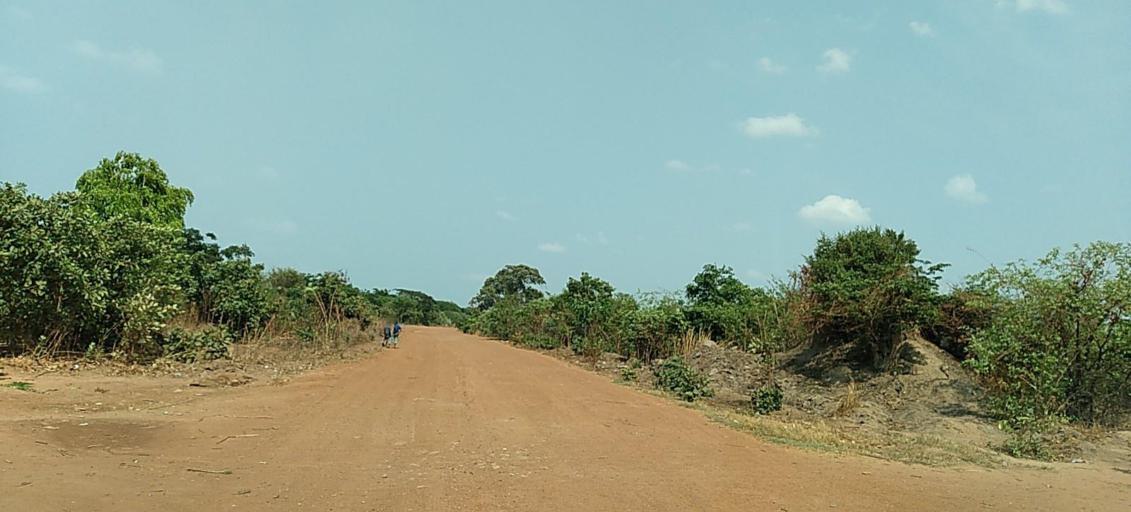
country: ZM
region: Copperbelt
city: Luanshya
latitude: -13.0925
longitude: 28.3071
